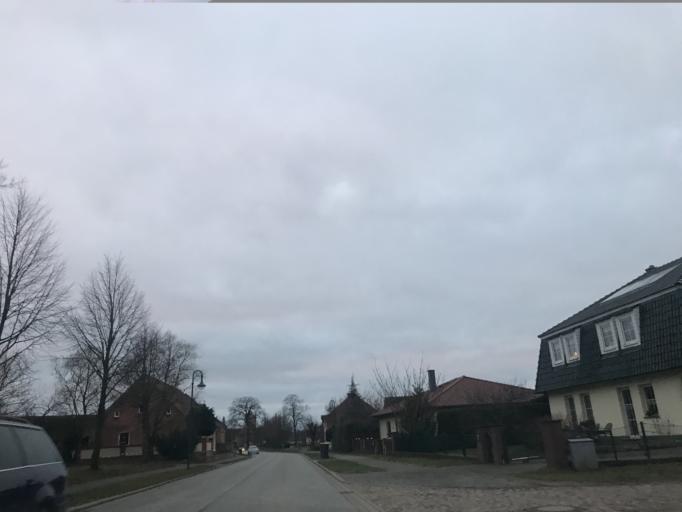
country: DE
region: Brandenburg
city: Wittstock
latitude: 53.1698
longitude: 12.5401
